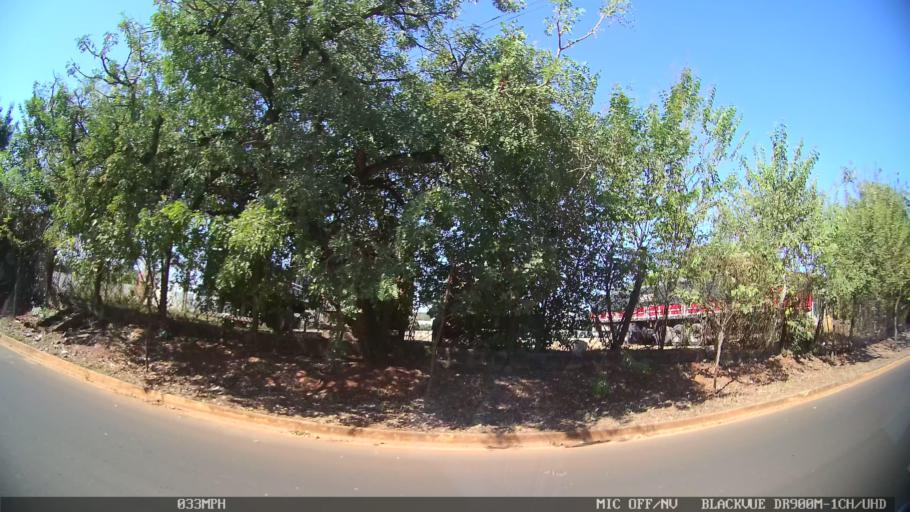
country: BR
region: Sao Paulo
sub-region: Ribeirao Preto
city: Ribeirao Preto
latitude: -21.2189
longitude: -47.7622
